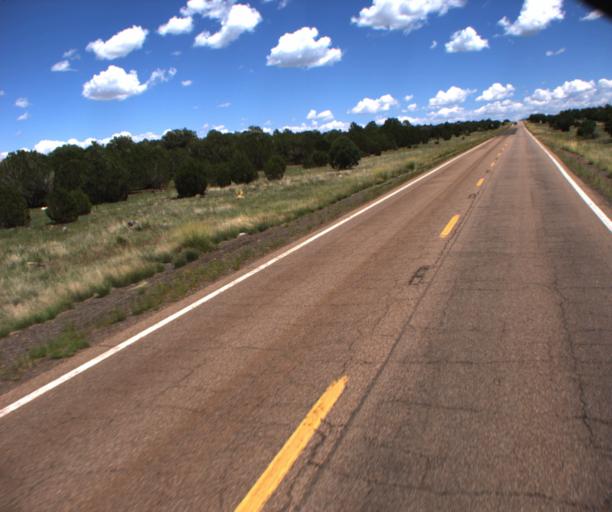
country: US
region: Arizona
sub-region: Navajo County
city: Pinetop-Lakeside
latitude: 34.2743
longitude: -109.7696
